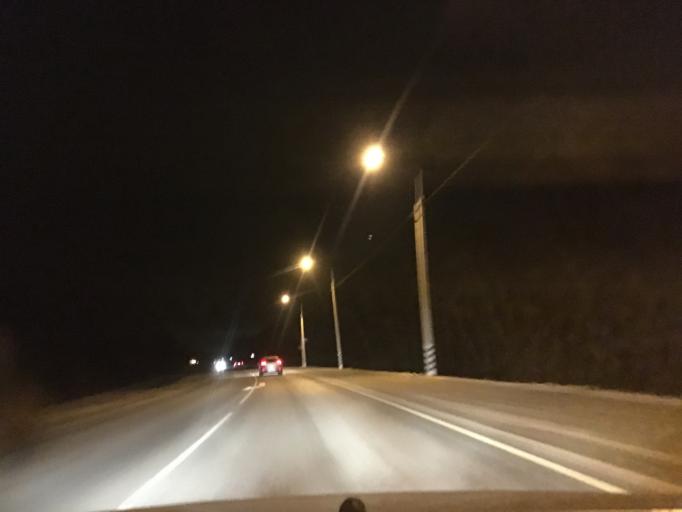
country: RU
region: Tula
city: Pervomayskiy
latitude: 54.0541
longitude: 37.5319
